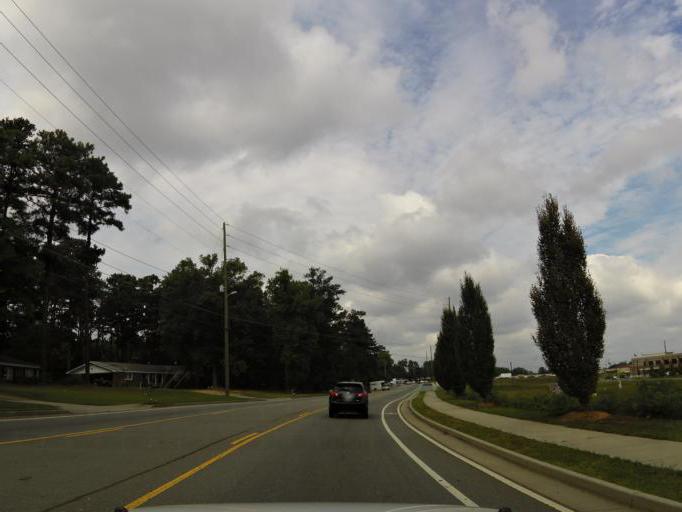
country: US
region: Georgia
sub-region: Cobb County
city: Kennesaw
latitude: 34.0123
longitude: -84.6173
